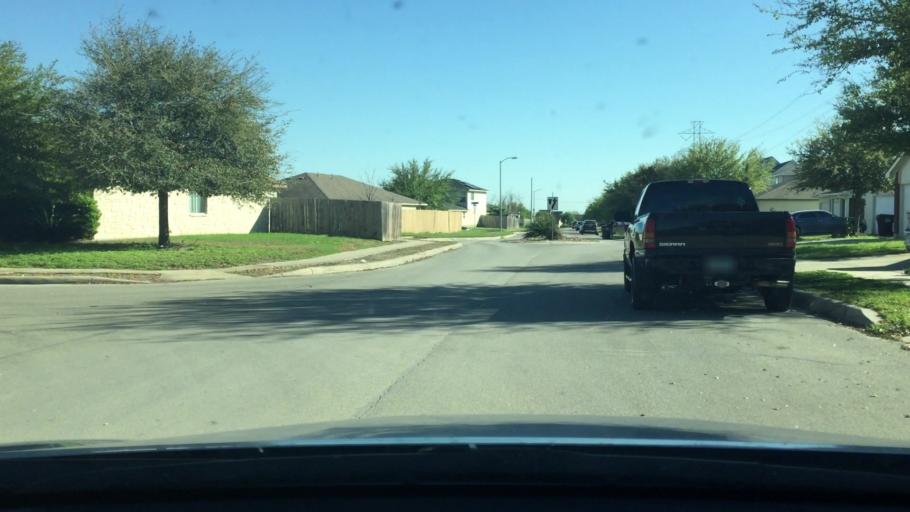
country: US
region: Texas
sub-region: Bexar County
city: Converse
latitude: 29.4665
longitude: -98.3229
